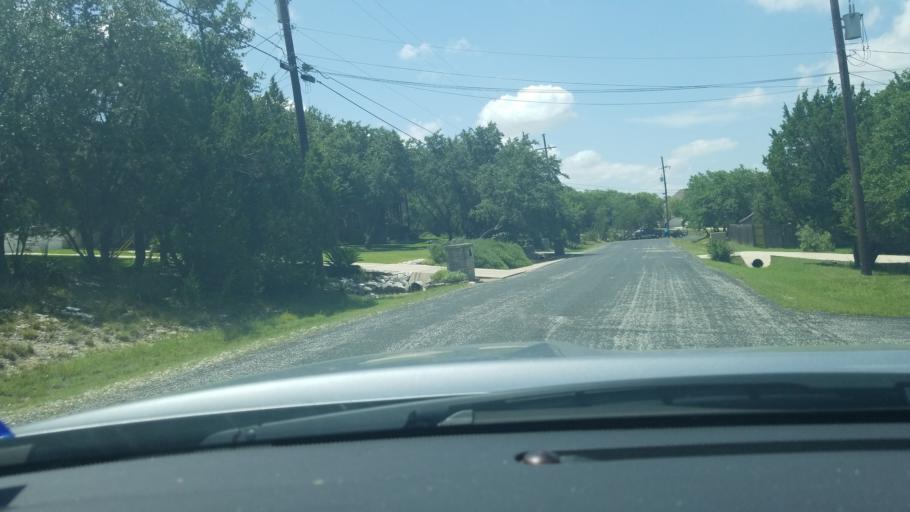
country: US
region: Texas
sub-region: Bexar County
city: Timberwood Park
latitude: 29.6904
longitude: -98.4852
